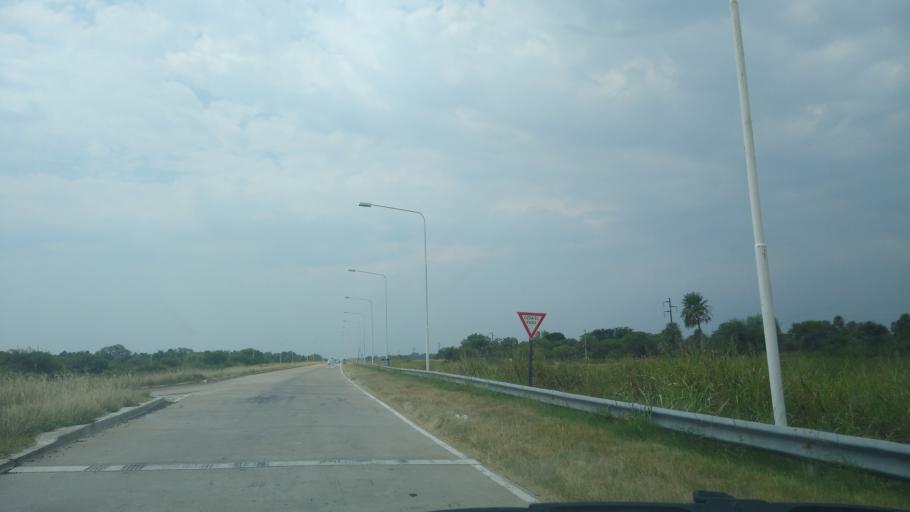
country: AR
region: Chaco
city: Margarita Belen
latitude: -27.0884
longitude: -58.9576
